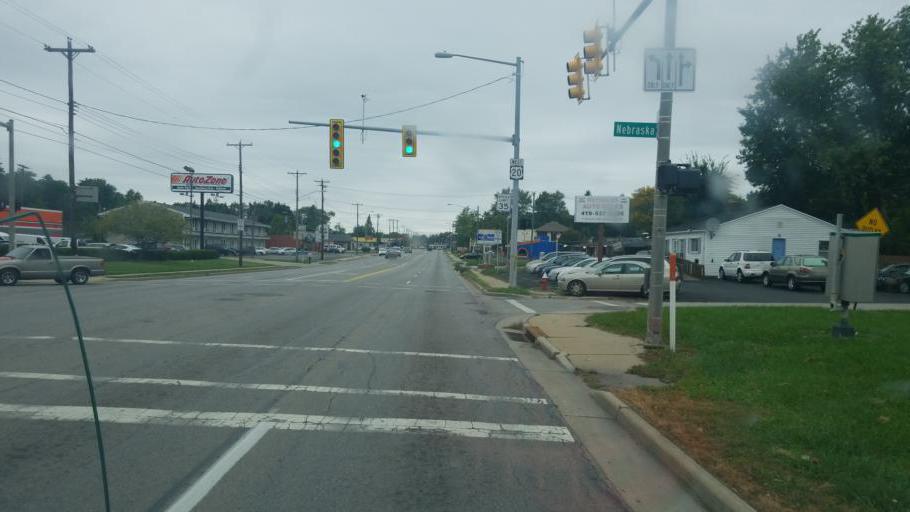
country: US
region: Ohio
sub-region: Lucas County
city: Ottawa Hills
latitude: 41.6458
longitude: -83.6645
